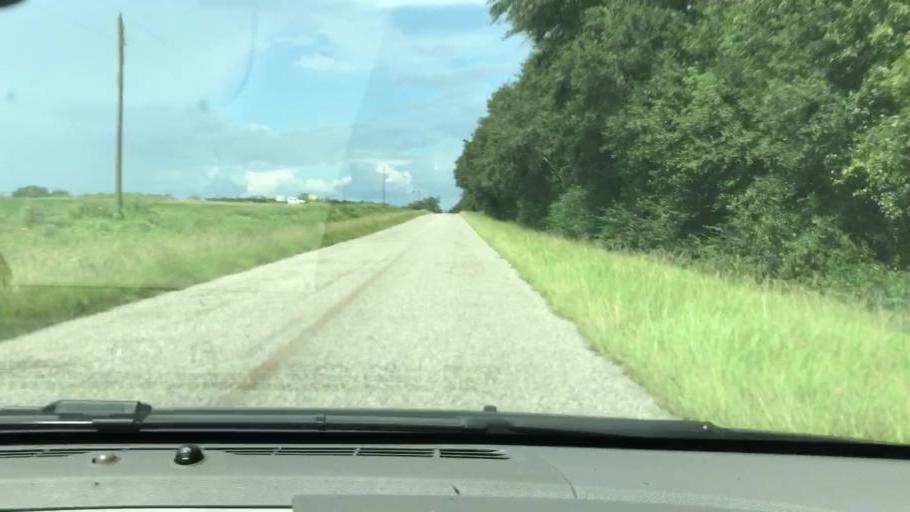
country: US
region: Georgia
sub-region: Early County
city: Blakely
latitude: 31.2085
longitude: -85.0034
